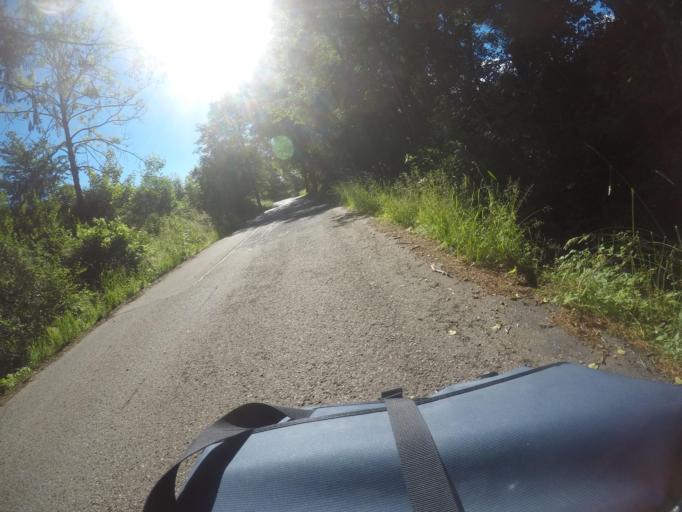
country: DE
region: Bavaria
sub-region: Swabia
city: Nesselwang
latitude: 47.6283
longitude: 10.4796
